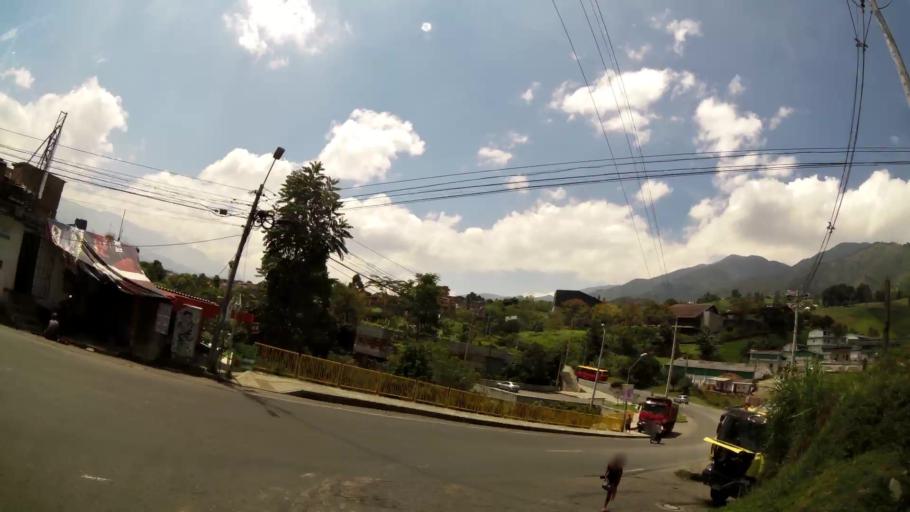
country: CO
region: Antioquia
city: La Estrella
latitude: 6.1786
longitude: -75.6534
